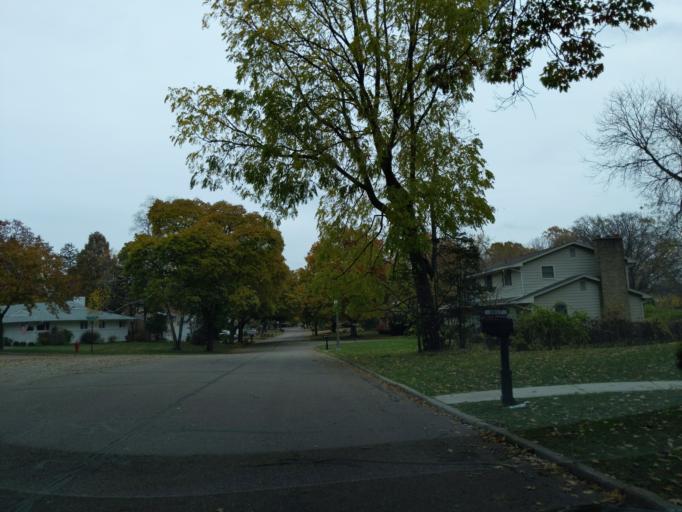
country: US
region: Michigan
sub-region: Ingham County
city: Edgemont Park
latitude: 42.7128
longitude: -84.5917
